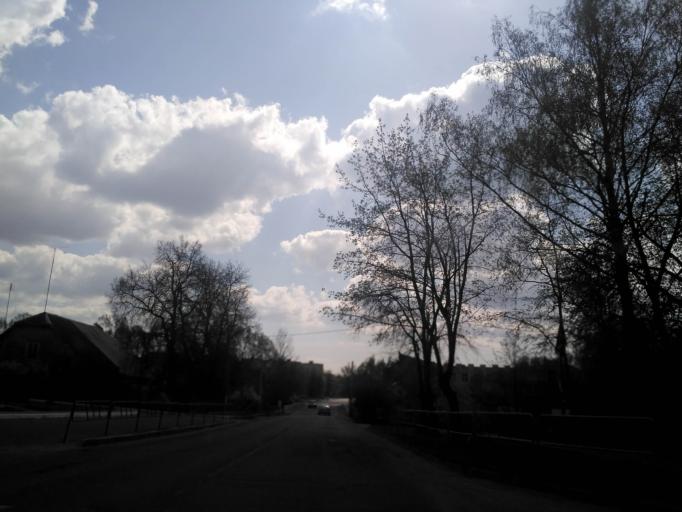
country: BY
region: Minsk
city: Radashkovichy
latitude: 54.1582
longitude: 27.2391
